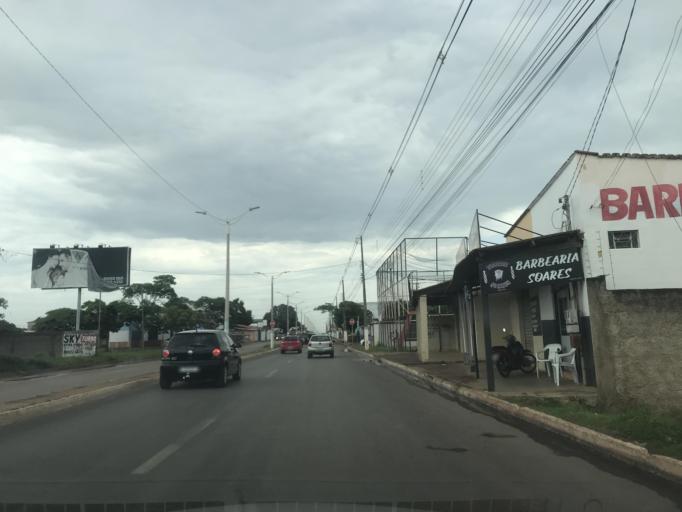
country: BR
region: Goias
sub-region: Luziania
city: Luziania
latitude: -16.2062
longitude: -47.9257
